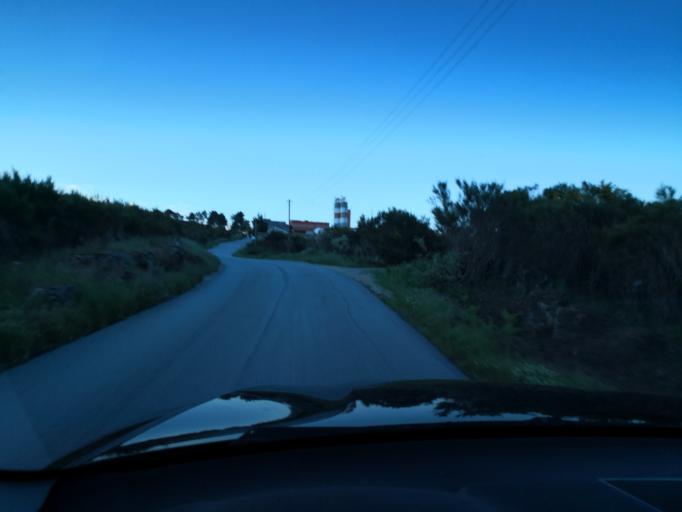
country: PT
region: Vila Real
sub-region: Vila Real
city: Vila Real
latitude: 41.3417
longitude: -7.6957
